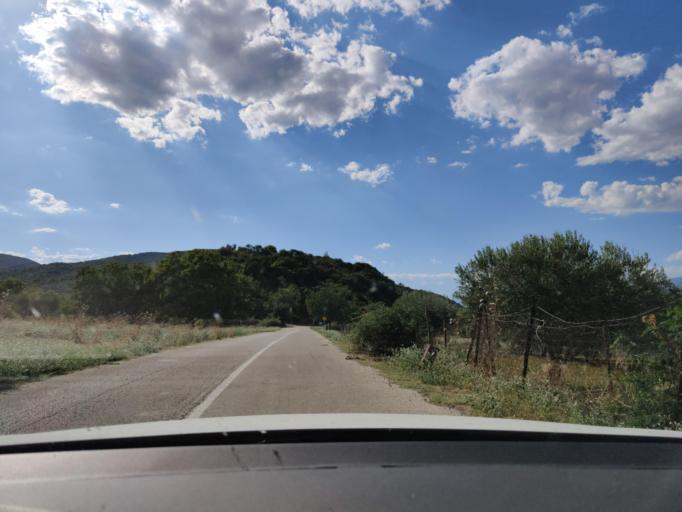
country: GR
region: Central Macedonia
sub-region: Nomos Serron
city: Chrysochorafa
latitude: 41.1620
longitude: 23.1857
